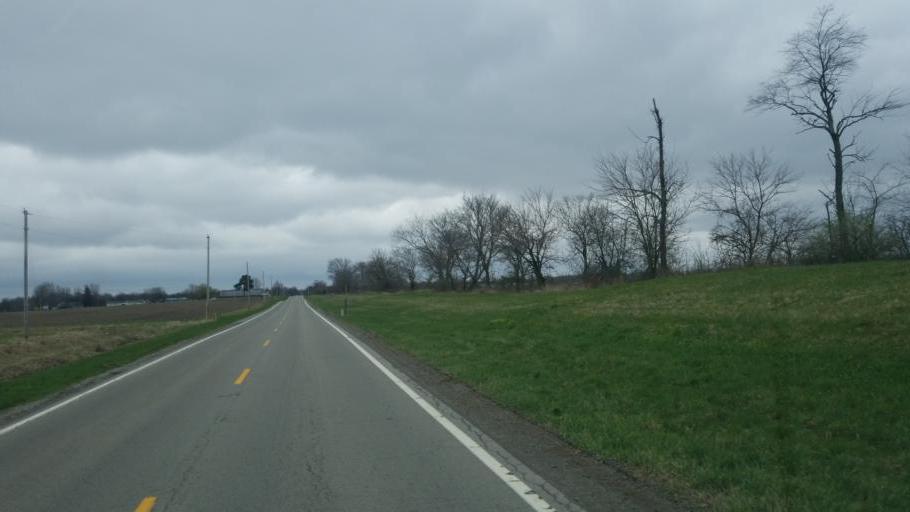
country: US
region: Ohio
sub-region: Hardin County
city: Kenton
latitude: 40.6711
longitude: -83.5986
